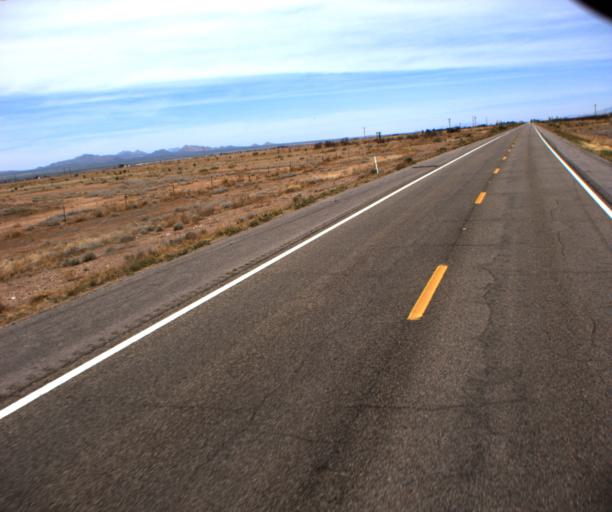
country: US
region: Arizona
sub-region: Cochise County
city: Pirtleville
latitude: 31.5657
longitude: -109.6677
